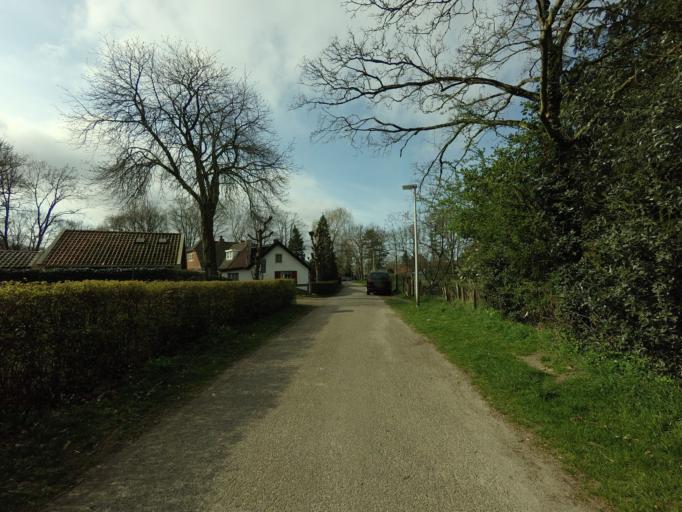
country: NL
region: North Holland
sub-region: Gemeente Laren
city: Laren
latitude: 52.2599
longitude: 5.2354
